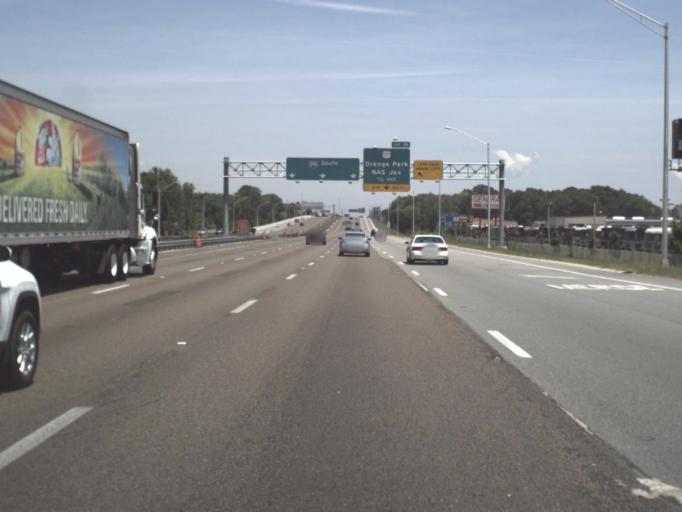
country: US
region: Florida
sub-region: Clay County
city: Bellair-Meadowbrook Terrace
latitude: 30.1911
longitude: -81.7204
